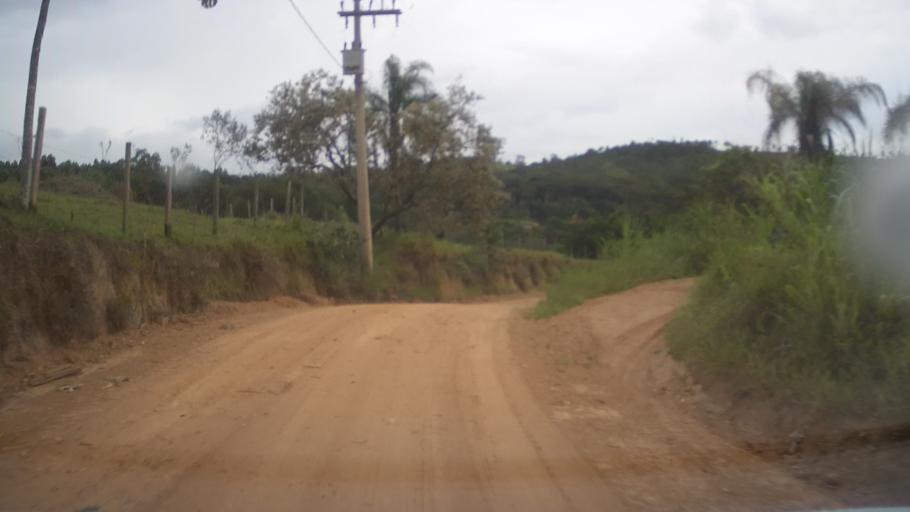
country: BR
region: Sao Paulo
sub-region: Itupeva
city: Itupeva
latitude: -23.1985
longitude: -47.0548
